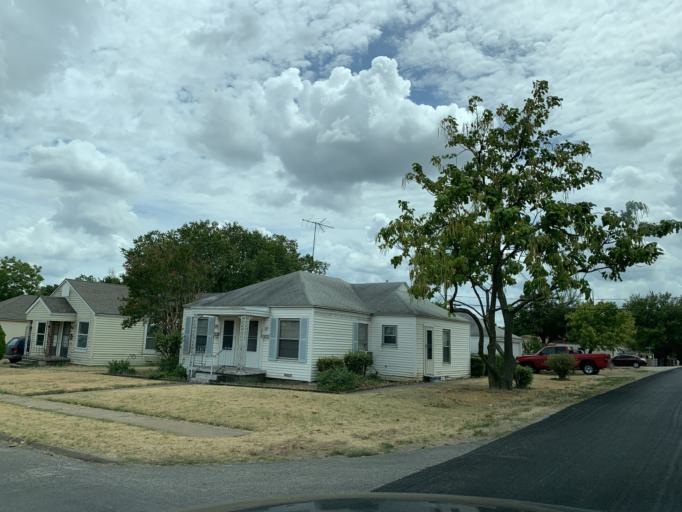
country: US
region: Texas
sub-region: Dallas County
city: Cockrell Hill
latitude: 32.7454
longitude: -96.8806
